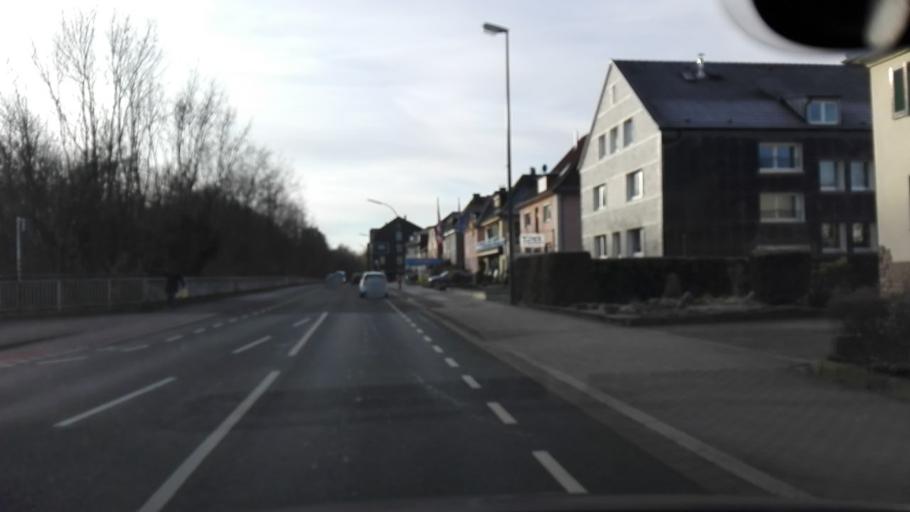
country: DE
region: North Rhine-Westphalia
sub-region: Regierungsbezirk Arnsberg
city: Dortmund
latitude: 51.5076
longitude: 7.4217
